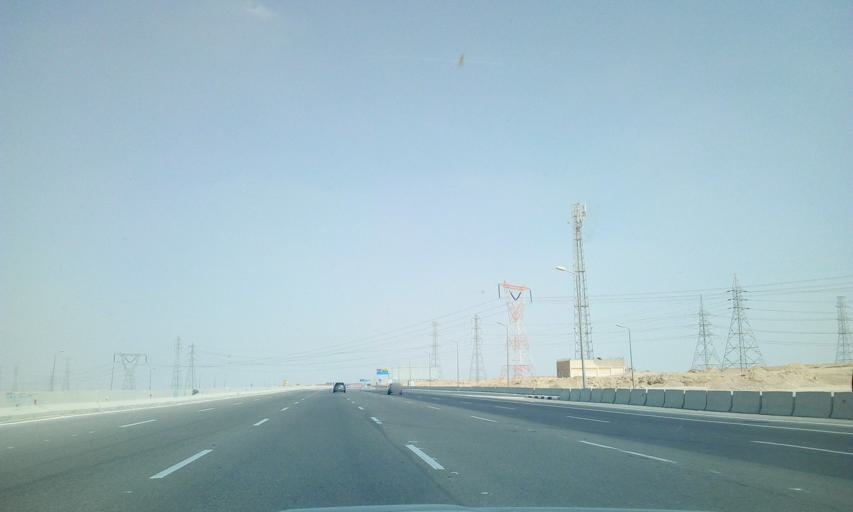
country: EG
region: Muhafazat al Qahirah
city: Halwan
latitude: 29.9064
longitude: 31.6801
